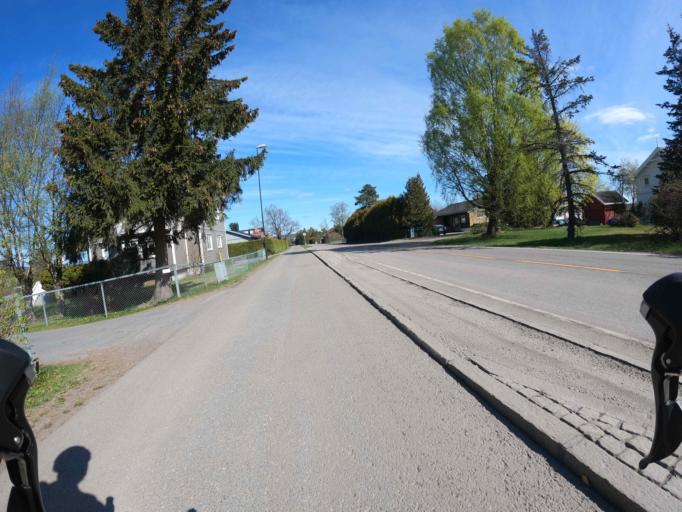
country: NO
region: Akershus
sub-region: Skedsmo
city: Lillestrom
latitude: 59.9637
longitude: 11.0088
